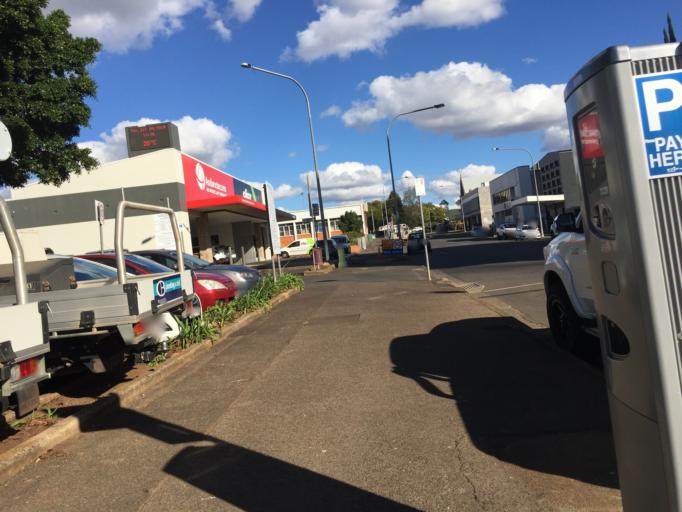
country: AU
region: Queensland
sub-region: Toowoomba
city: Toowoomba
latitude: -27.5636
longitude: 151.9541
